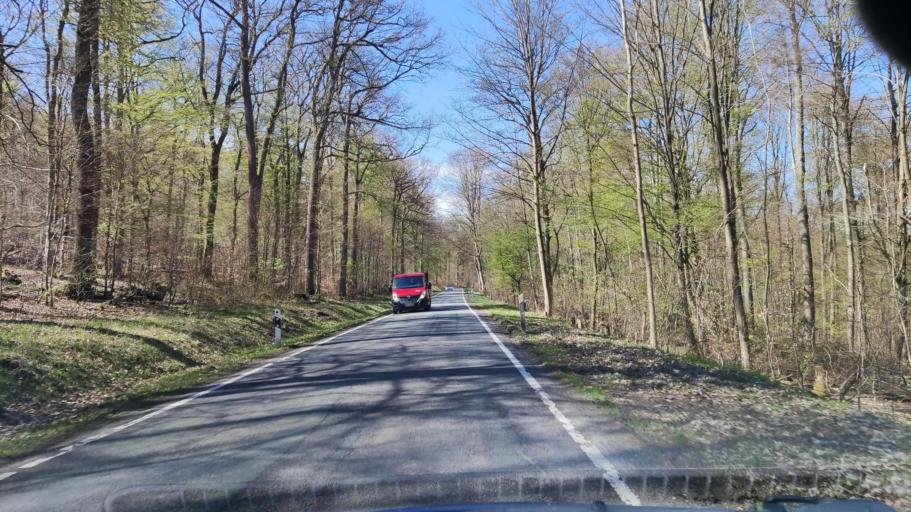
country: DE
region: Lower Saxony
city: Eimen
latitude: 51.9023
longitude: 9.7906
